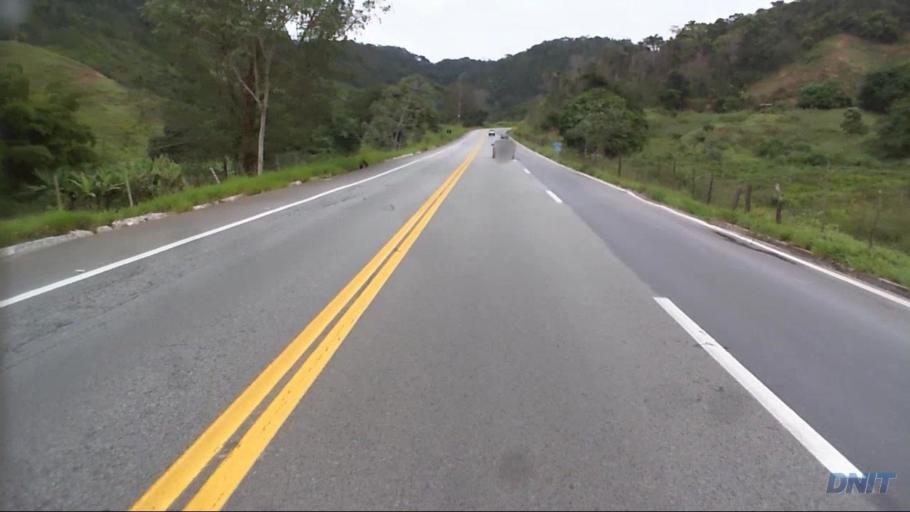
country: BR
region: Minas Gerais
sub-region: Timoteo
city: Timoteo
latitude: -19.6245
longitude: -42.8591
